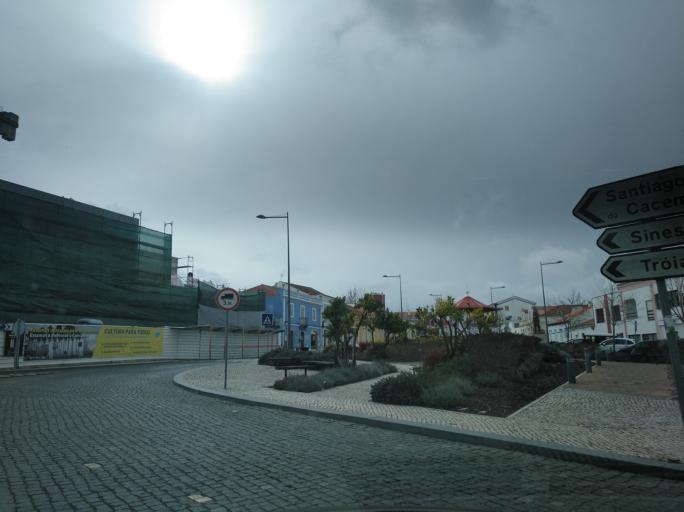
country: PT
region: Setubal
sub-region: Grandola
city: Grandola
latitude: 38.1771
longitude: -8.5671
